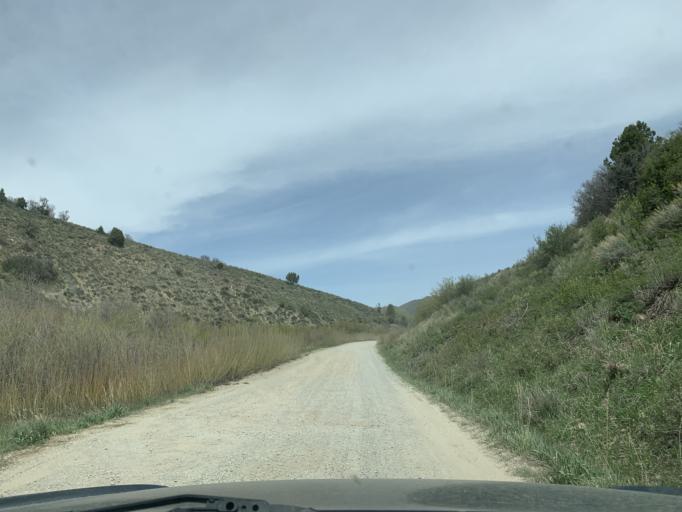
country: US
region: Utah
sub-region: Utah County
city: Mapleton
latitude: 40.1673
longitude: -111.3306
